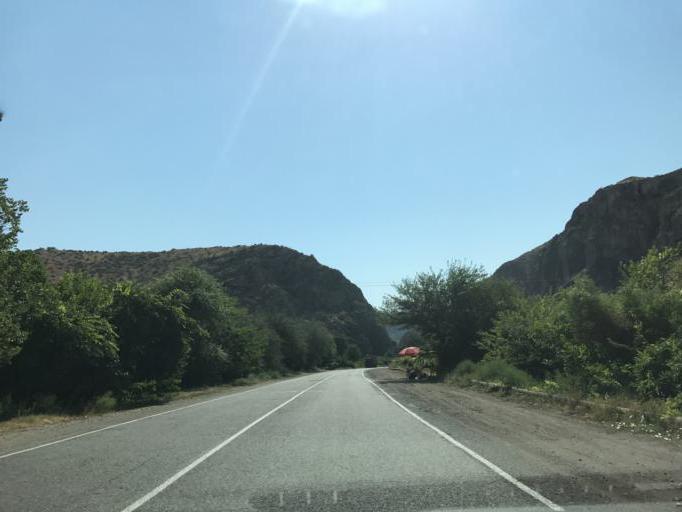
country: AM
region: Vayots' Dzori Marz
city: Areni
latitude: 39.7332
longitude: 45.1974
